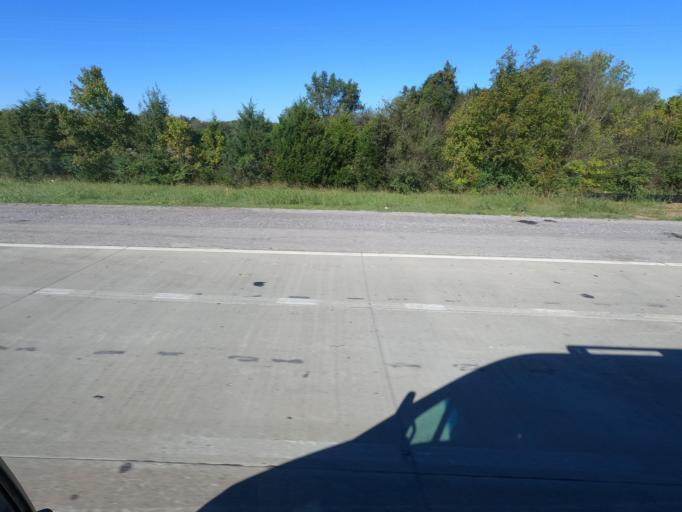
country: US
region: Tennessee
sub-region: Rutherford County
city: Smyrna
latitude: 35.9808
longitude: -86.4426
